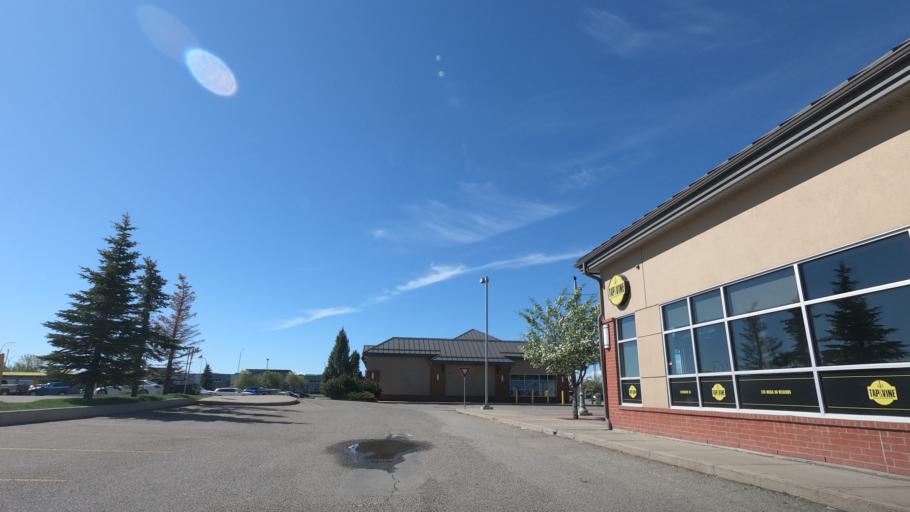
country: CA
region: Alberta
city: Airdrie
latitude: 51.2723
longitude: -113.9919
